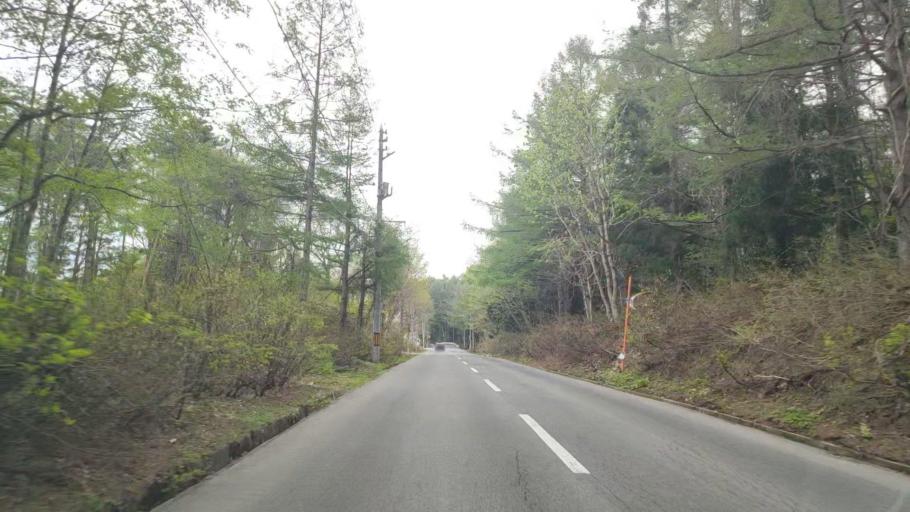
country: JP
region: Aomori
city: Aomori Shi
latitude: 40.7462
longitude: 140.8231
